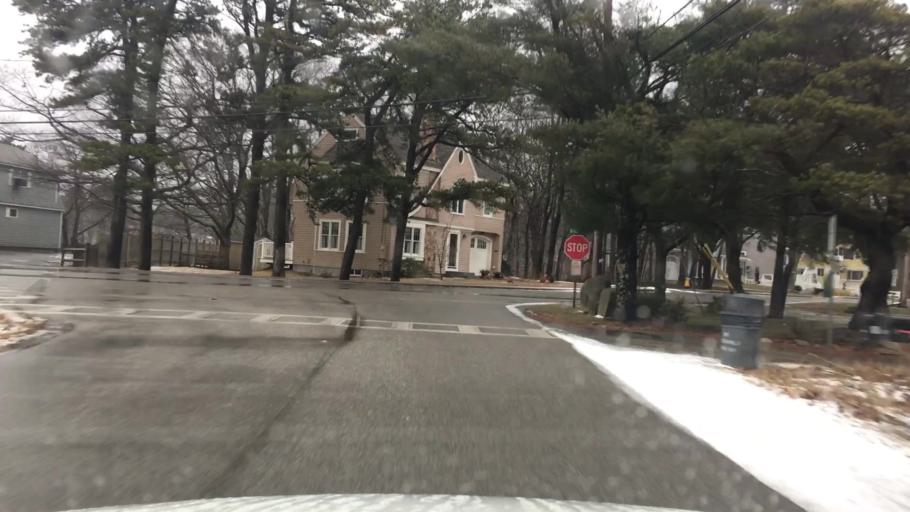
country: US
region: Maine
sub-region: York County
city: Arundel
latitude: 43.3984
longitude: -70.4174
